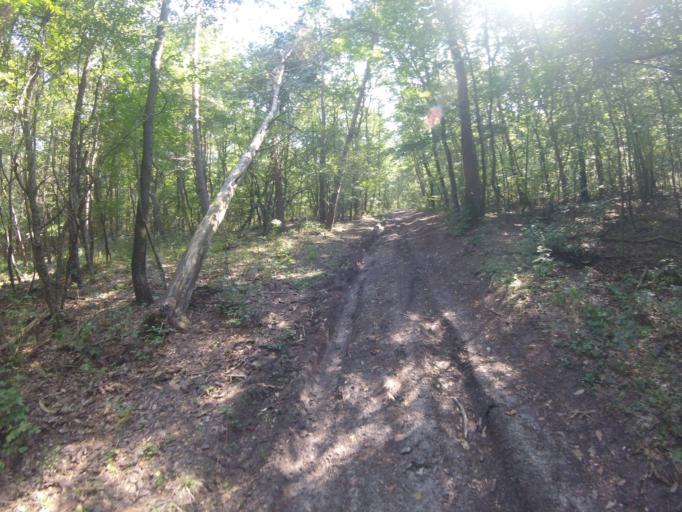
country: HU
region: Nograd
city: Bujak
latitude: 47.8961
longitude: 19.5375
